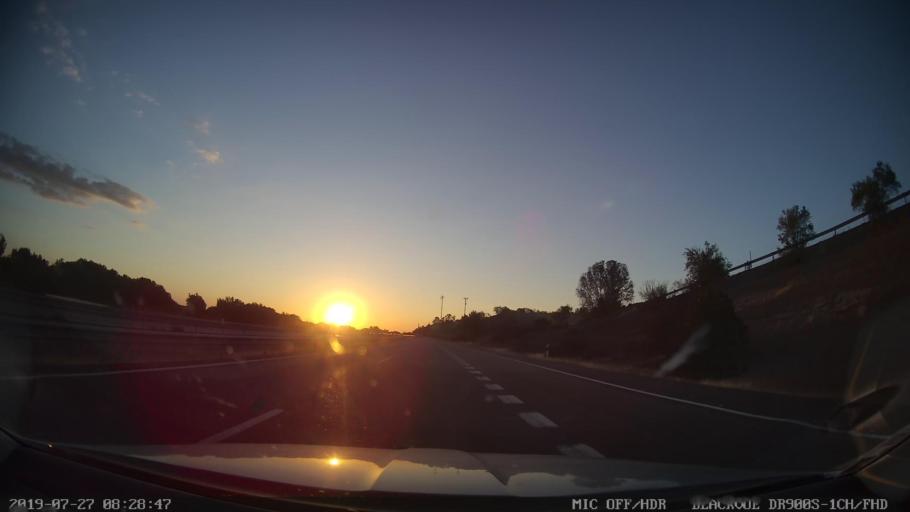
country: ES
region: Extremadura
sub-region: Provincia de Badajoz
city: Valdelacalzada
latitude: 38.8468
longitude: -6.6782
